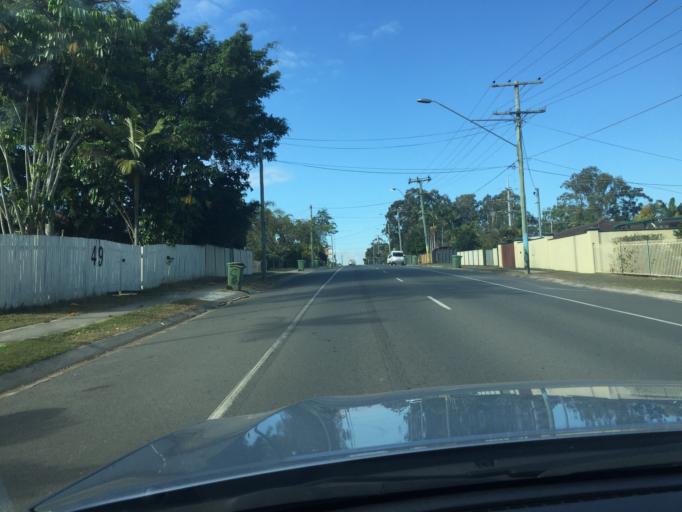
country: AU
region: Queensland
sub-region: Logan
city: Slacks Creek
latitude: -27.6413
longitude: 153.1539
